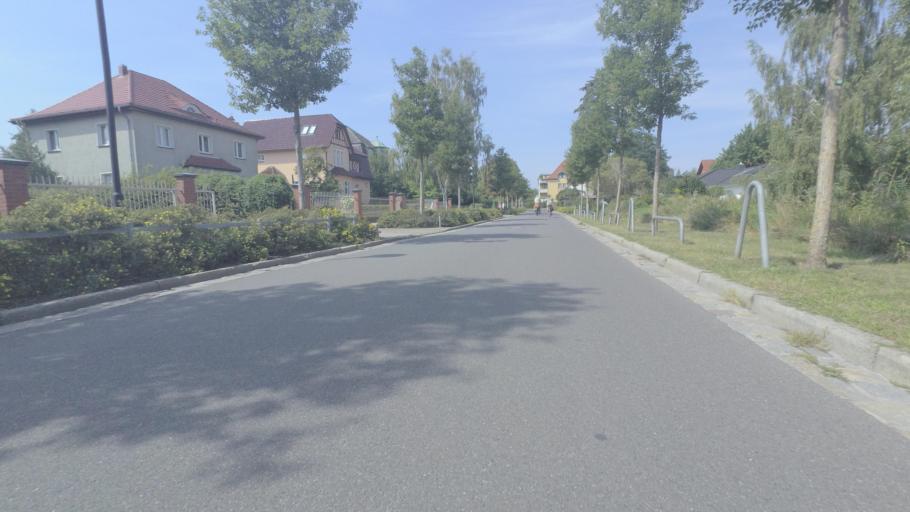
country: DE
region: Mecklenburg-Vorpommern
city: Waren
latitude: 53.5179
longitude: 12.6692
